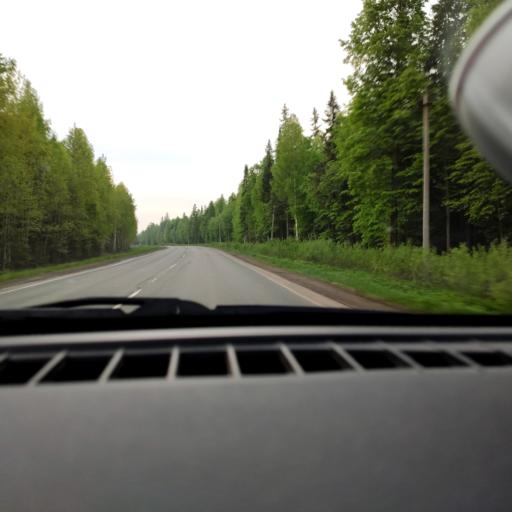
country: RU
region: Perm
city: Perm
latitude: 58.2179
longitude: 56.1706
